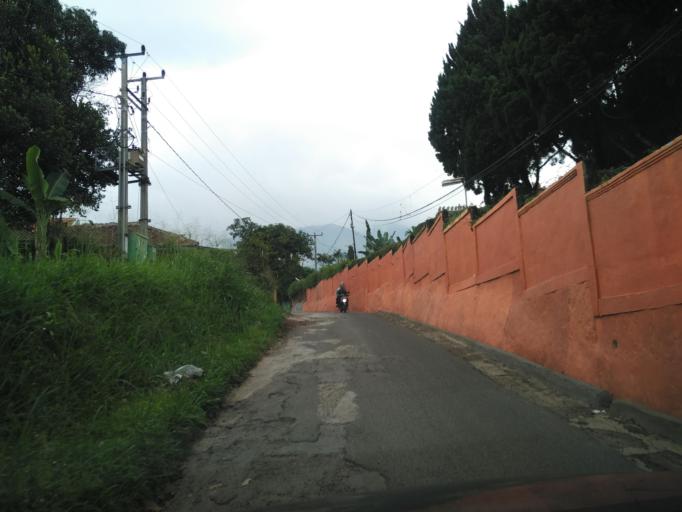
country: ID
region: West Java
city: Caringin
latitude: -6.6991
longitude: 107.0370
